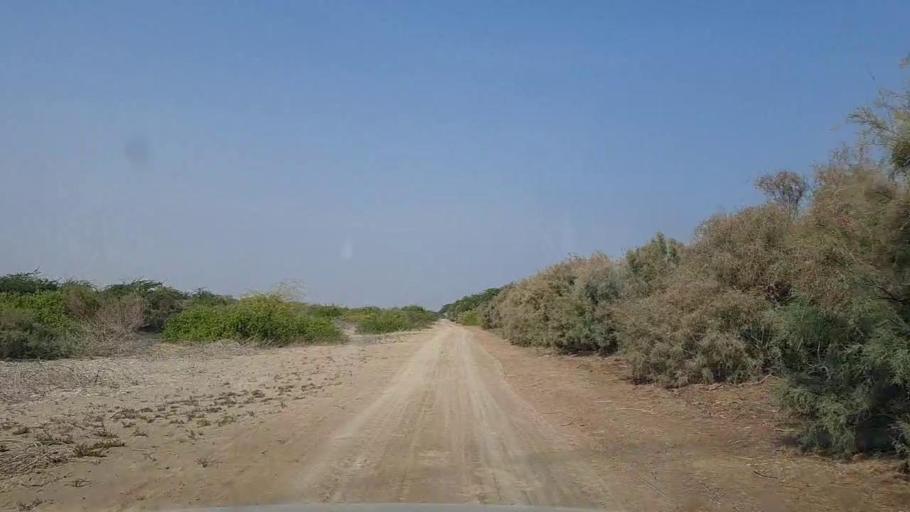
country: PK
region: Sindh
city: Mirpur Sakro
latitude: 24.5506
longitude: 67.5566
